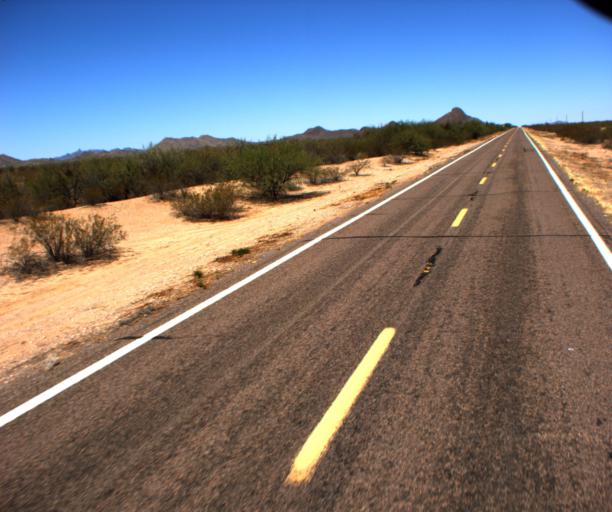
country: US
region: Arizona
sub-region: Pima County
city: Ajo
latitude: 32.2002
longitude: -112.4950
